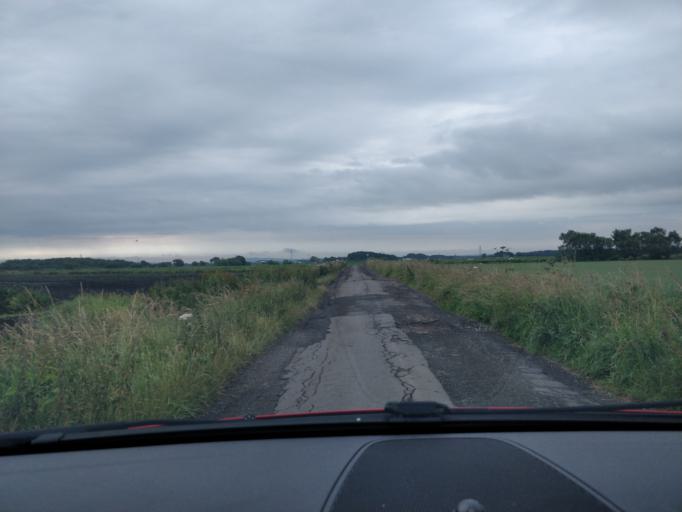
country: GB
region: England
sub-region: Lancashire
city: Banks
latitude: 53.6627
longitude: -2.9341
